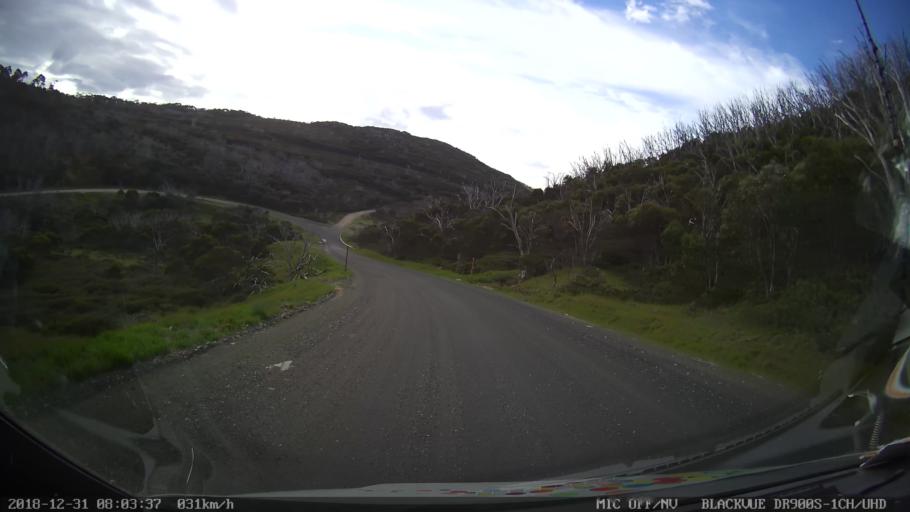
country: AU
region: New South Wales
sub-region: Snowy River
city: Jindabyne
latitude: -36.3651
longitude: 148.4033
